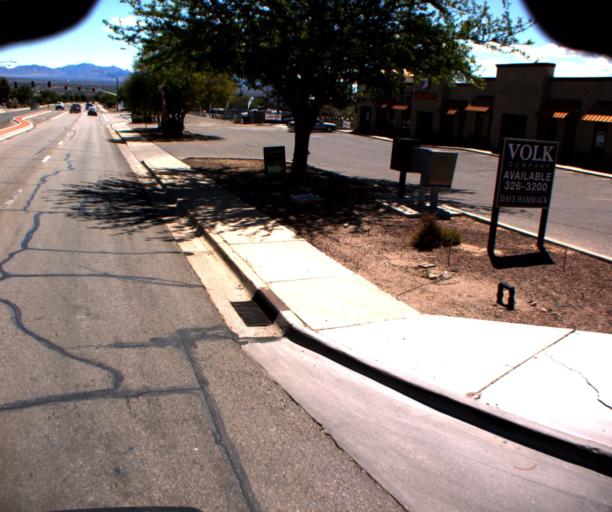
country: US
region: Arizona
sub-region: Cochise County
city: Benson
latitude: 31.9710
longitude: -110.3156
